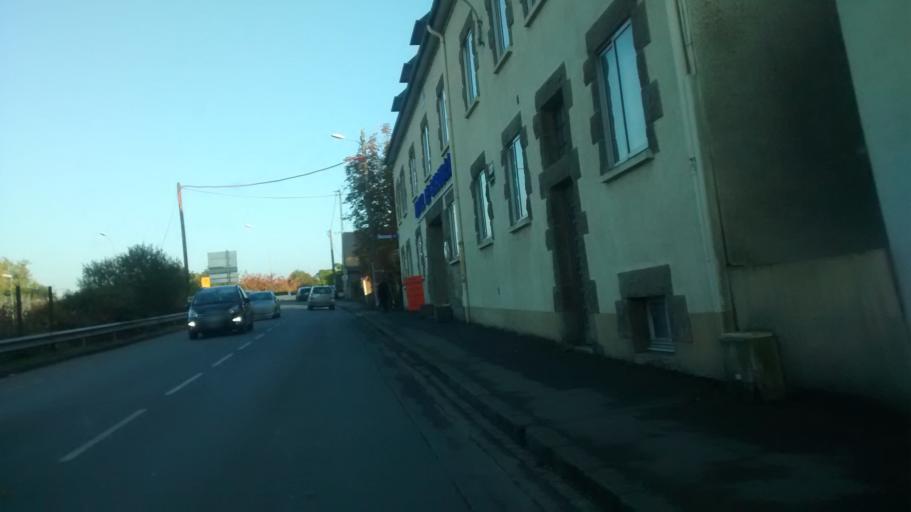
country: FR
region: Brittany
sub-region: Departement d'Ille-et-Vilaine
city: Le Rheu
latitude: 48.1228
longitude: -1.8197
